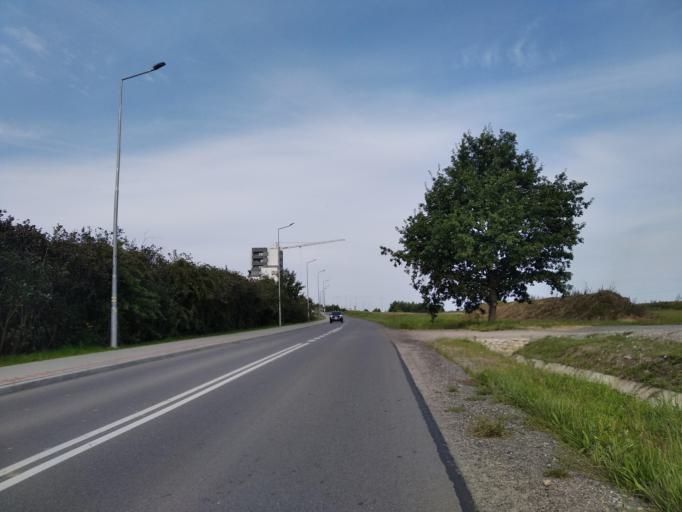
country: PL
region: Subcarpathian Voivodeship
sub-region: Powiat ropczycko-sedziszowski
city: Ropczyce
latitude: 50.0611
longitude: 21.6130
